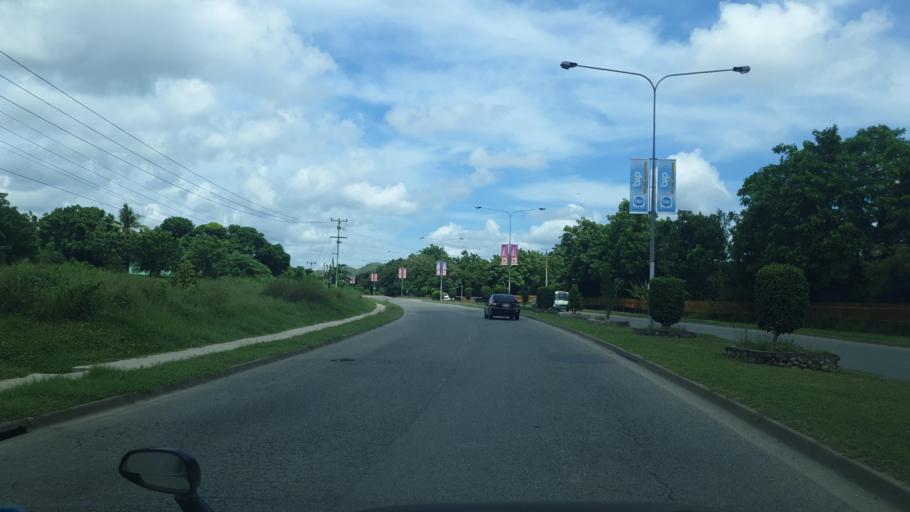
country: PG
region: National Capital
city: Port Moresby
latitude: -9.4048
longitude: 147.1644
